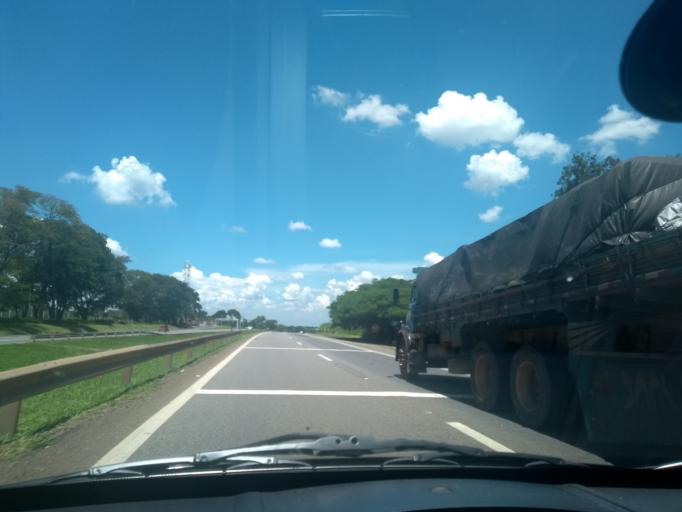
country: BR
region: Sao Paulo
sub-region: Mogi-Mirim
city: Mogi Mirim
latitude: -22.4885
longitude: -46.9813
